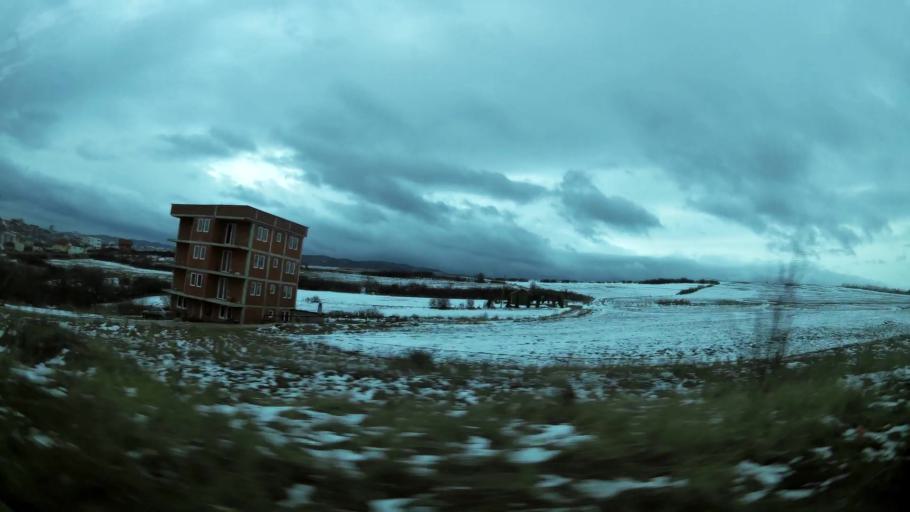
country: XK
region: Pristina
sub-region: Komuna e Prishtines
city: Pristina
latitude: 42.6365
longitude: 21.1655
